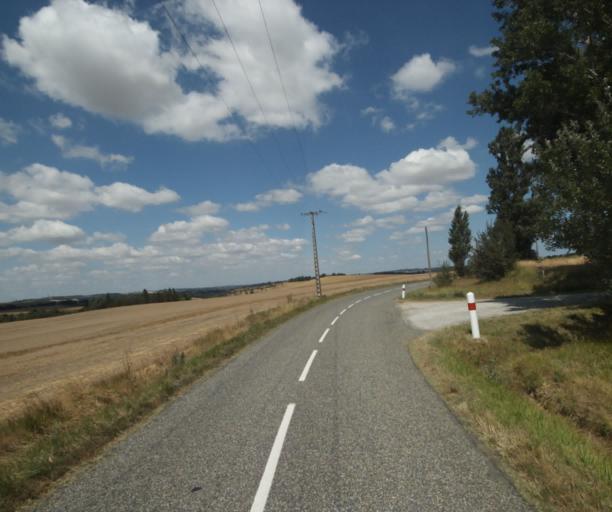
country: FR
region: Midi-Pyrenees
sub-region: Departement de la Haute-Garonne
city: Auriac-sur-Vendinelle
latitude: 43.4718
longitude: 1.8328
